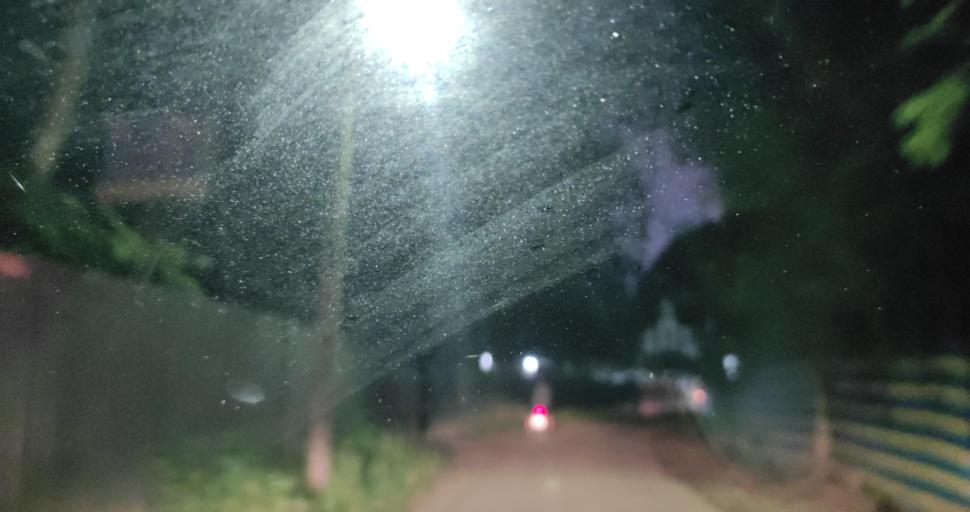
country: IN
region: Kerala
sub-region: Alappuzha
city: Shertallai
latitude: 9.6261
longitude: 76.3387
